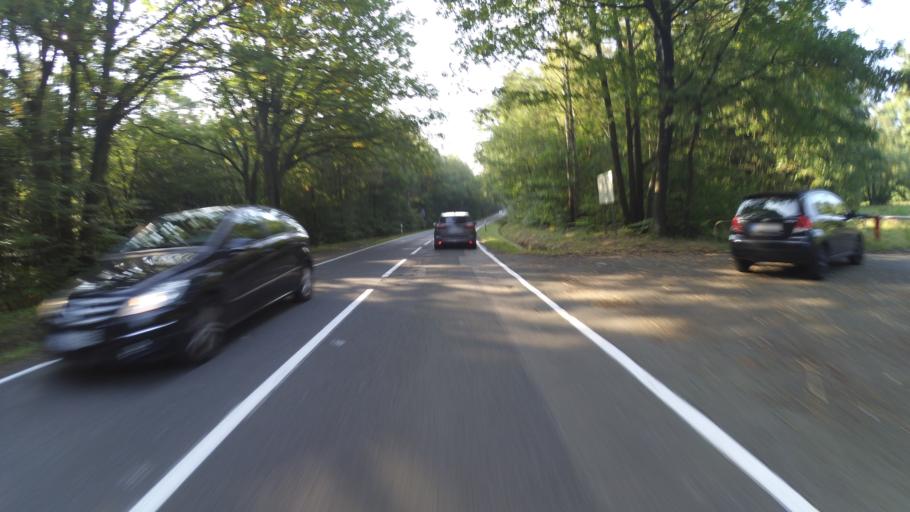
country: DE
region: Rheinland-Pfalz
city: Landstuhl
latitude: 49.4012
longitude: 7.5397
